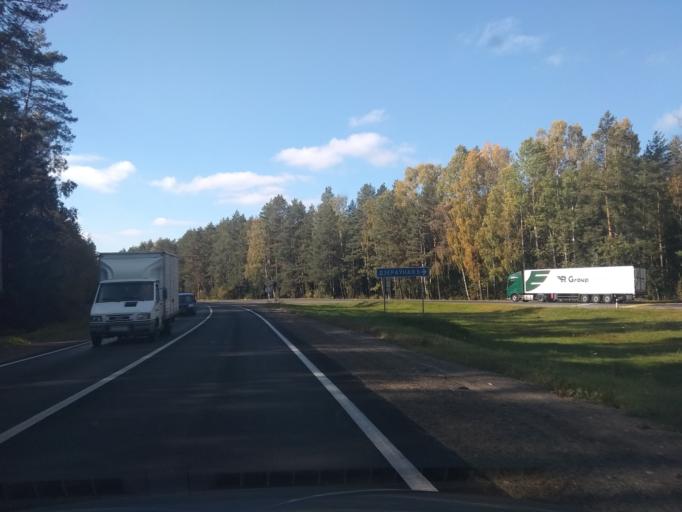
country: BY
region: Brest
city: Baranovichi
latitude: 53.0492
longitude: 25.8396
